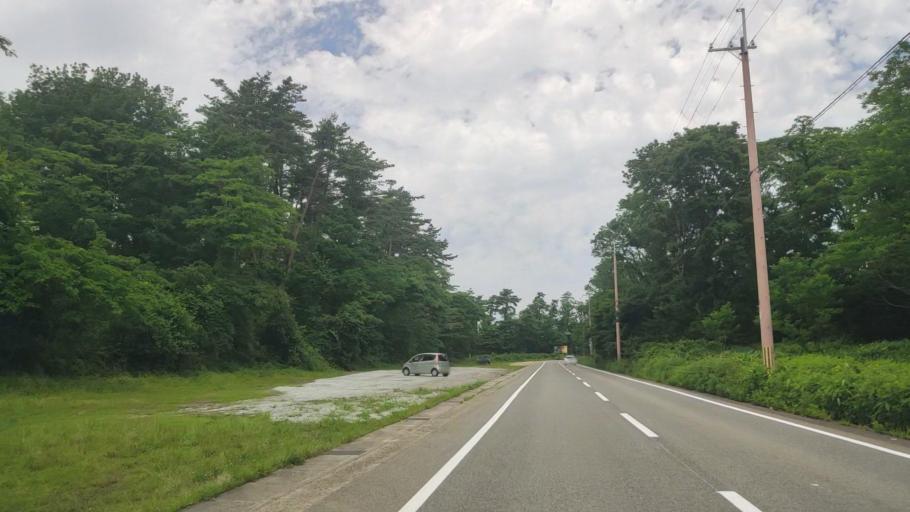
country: JP
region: Hyogo
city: Toyooka
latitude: 35.4982
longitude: 134.6833
